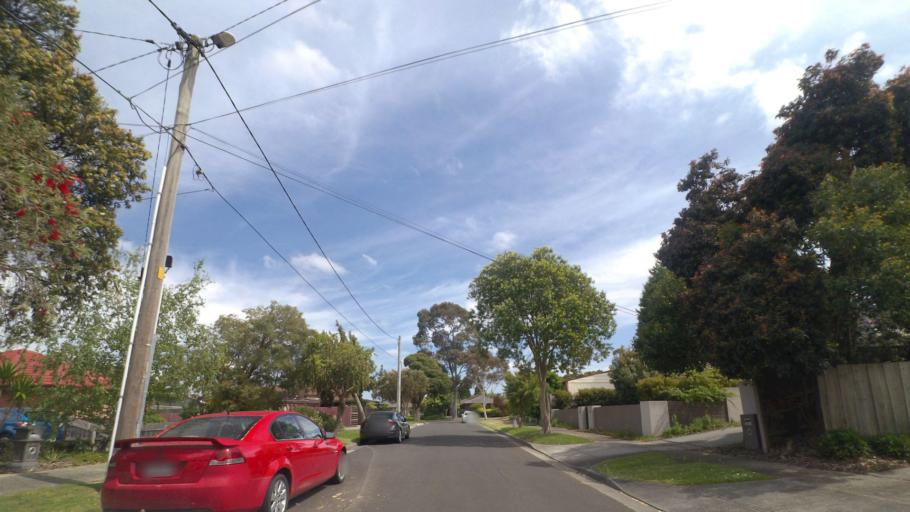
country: AU
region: Victoria
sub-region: Maroondah
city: Heathmont
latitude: -37.8525
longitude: 145.2462
